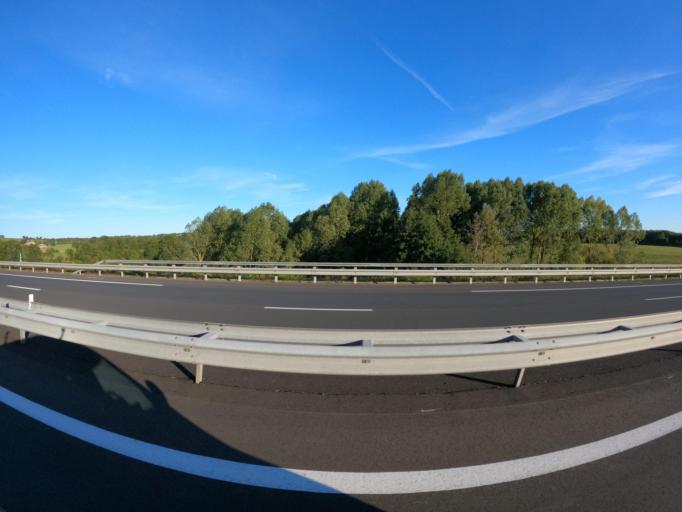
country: FR
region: Pays de la Loire
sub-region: Departement de la Vendee
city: La Gaubretiere
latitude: 46.9106
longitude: -1.0461
